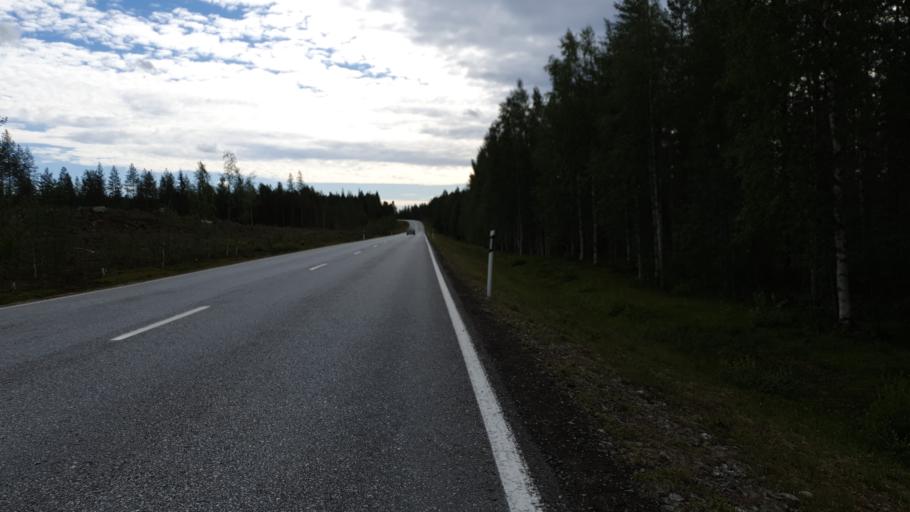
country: FI
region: Kainuu
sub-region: Kehys-Kainuu
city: Kuhmo
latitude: 64.4804
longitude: 29.7496
